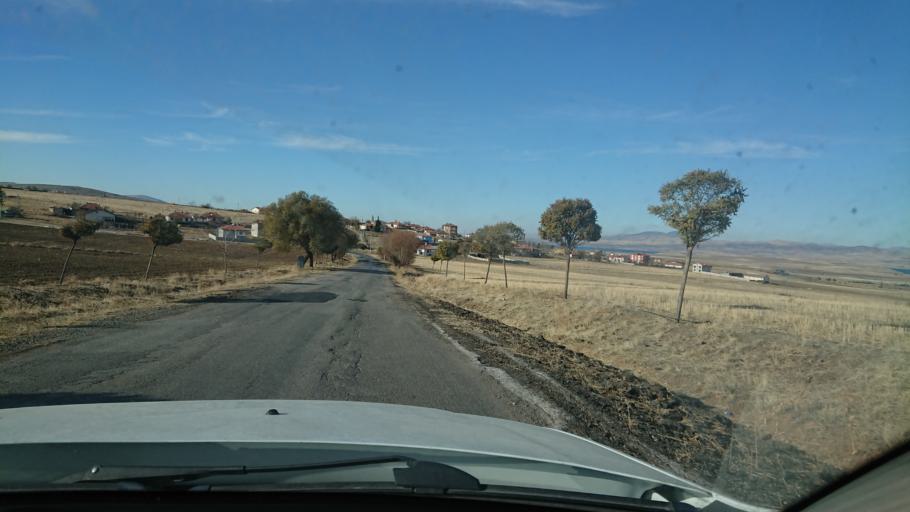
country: TR
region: Aksaray
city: Sariyahsi
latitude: 38.9759
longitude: 33.8571
